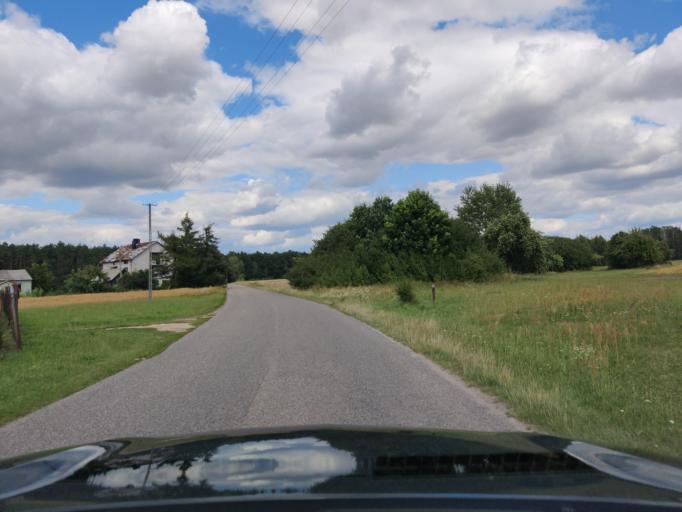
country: PL
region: Masovian Voivodeship
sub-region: Powiat wegrowski
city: Miedzna
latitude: 52.4885
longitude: 22.0259
